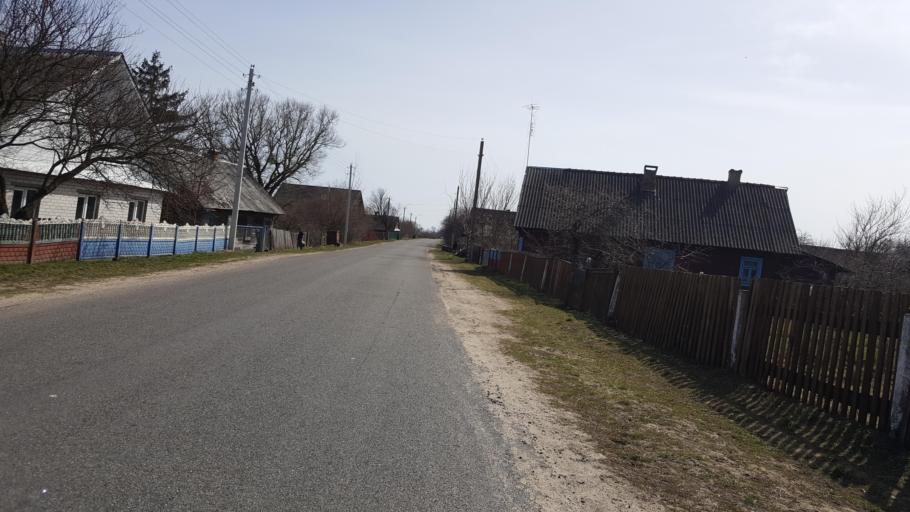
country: BY
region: Brest
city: Kamyanyuki
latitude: 52.4884
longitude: 23.8736
